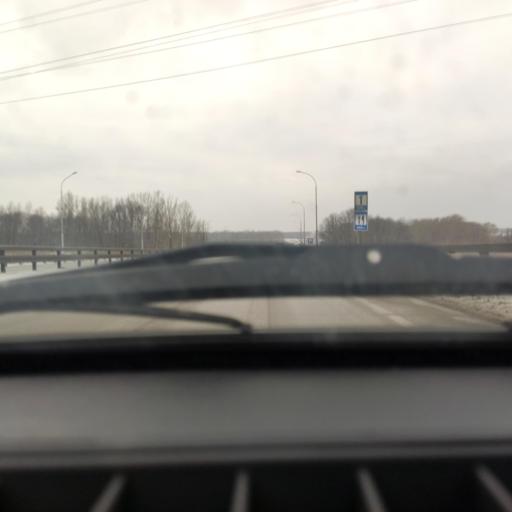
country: RU
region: Bashkortostan
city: Kabakovo
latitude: 54.6532
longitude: 56.1072
